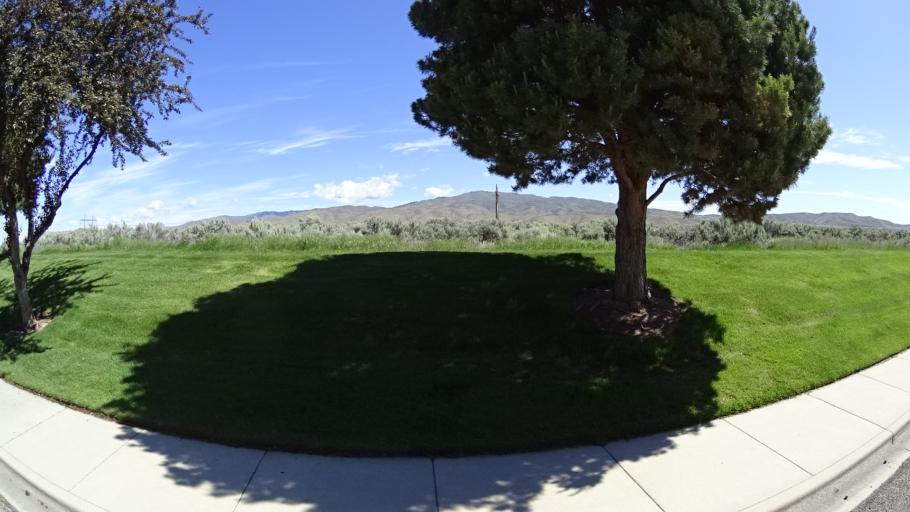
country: US
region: Idaho
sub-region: Ada County
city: Boise
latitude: 43.5491
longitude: -116.1208
